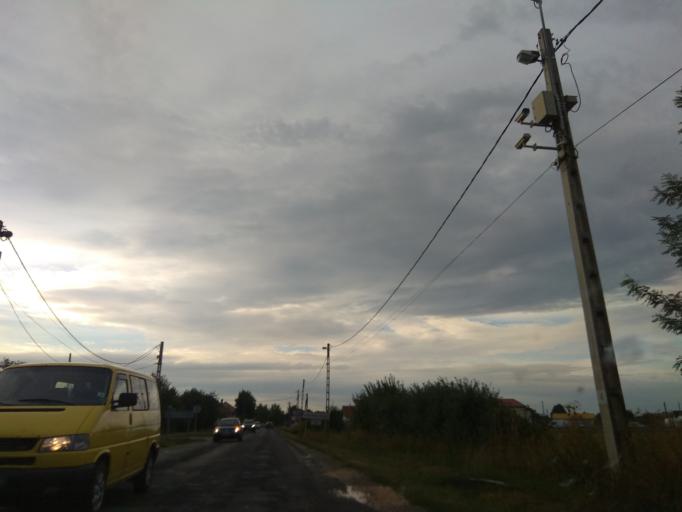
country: HU
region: Borsod-Abauj-Zemplen
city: Miskolc
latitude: 48.0846
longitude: 20.8180
